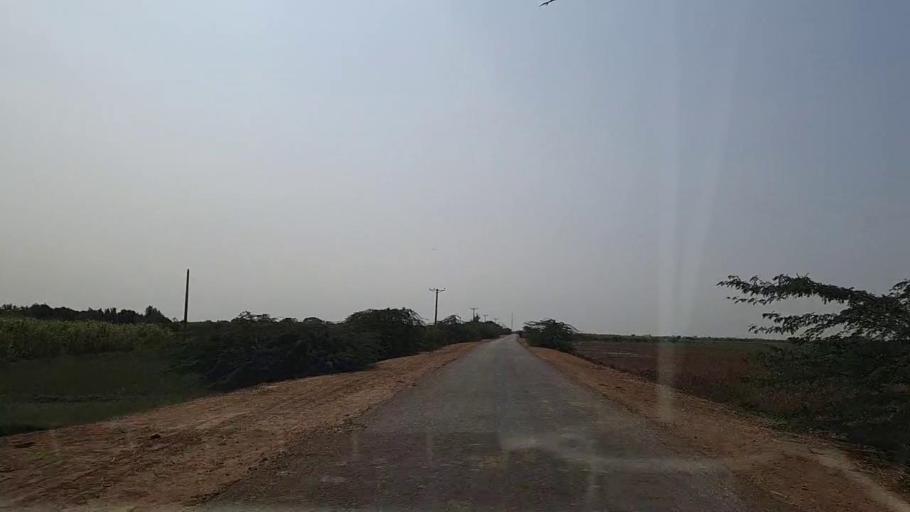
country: PK
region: Sindh
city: Chuhar Jamali
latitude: 24.2999
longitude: 67.9324
